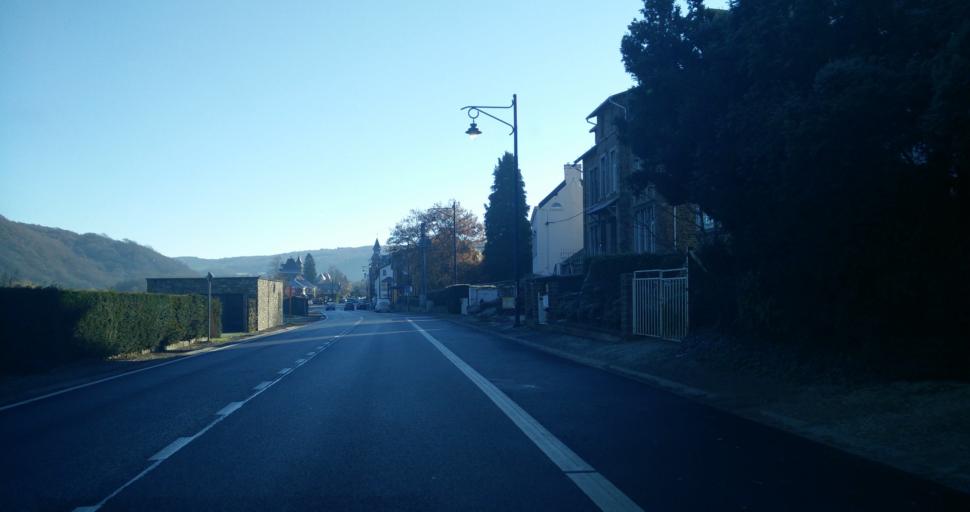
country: BE
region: Wallonia
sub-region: Province de Namur
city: Namur
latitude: 50.4252
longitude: 4.8712
